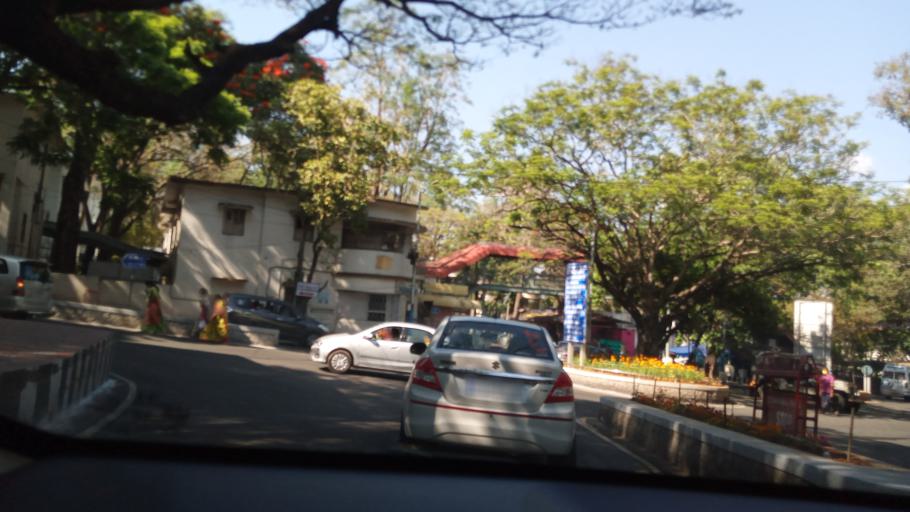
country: IN
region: Andhra Pradesh
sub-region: Chittoor
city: Tirumala
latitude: 13.6799
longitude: 79.3488
